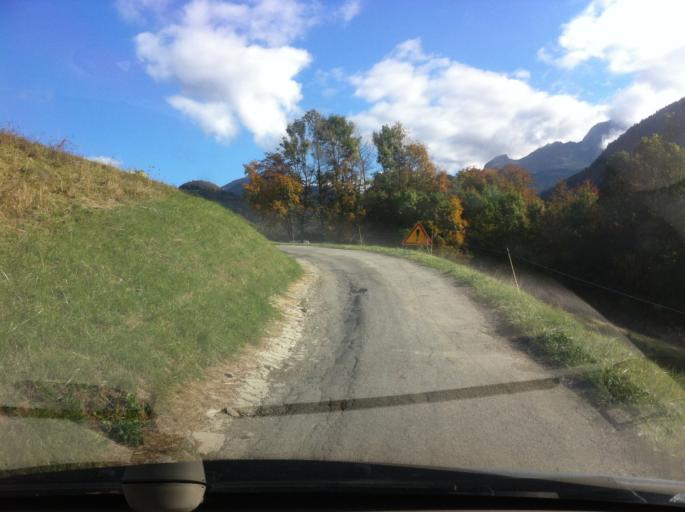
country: FR
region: Rhone-Alpes
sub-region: Departement de la Haute-Savoie
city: Faverges
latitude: 45.7780
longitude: 6.3056
